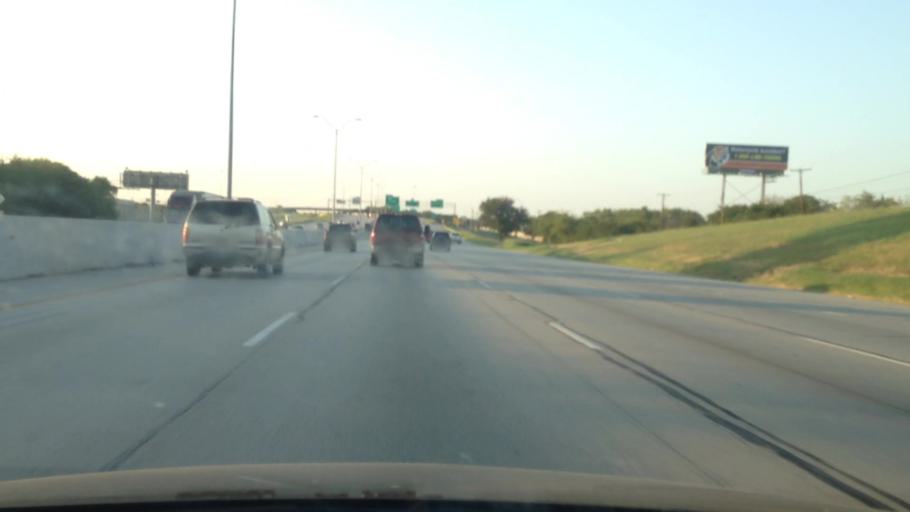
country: US
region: Texas
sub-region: Tarrant County
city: Forest Hill
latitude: 32.6833
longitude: -97.2404
